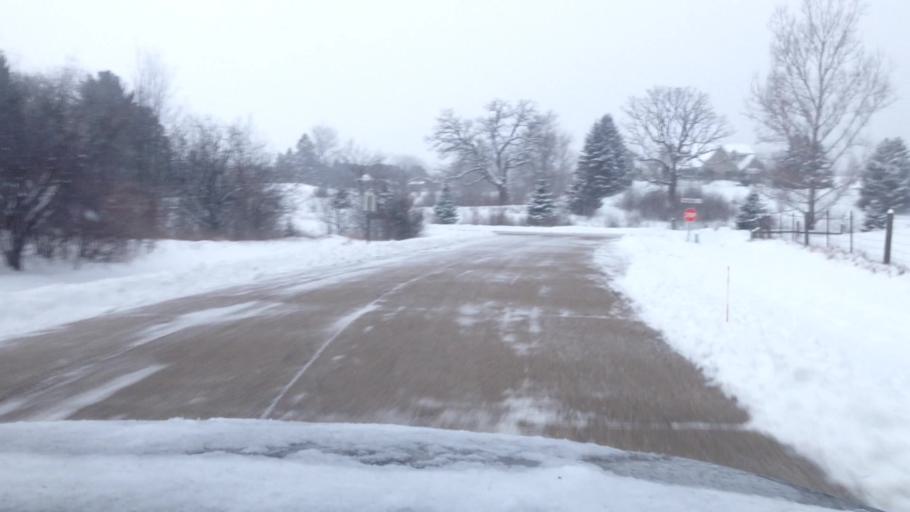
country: US
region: Wisconsin
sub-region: Waukesha County
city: North Prairie
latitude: 42.9464
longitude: -88.4152
